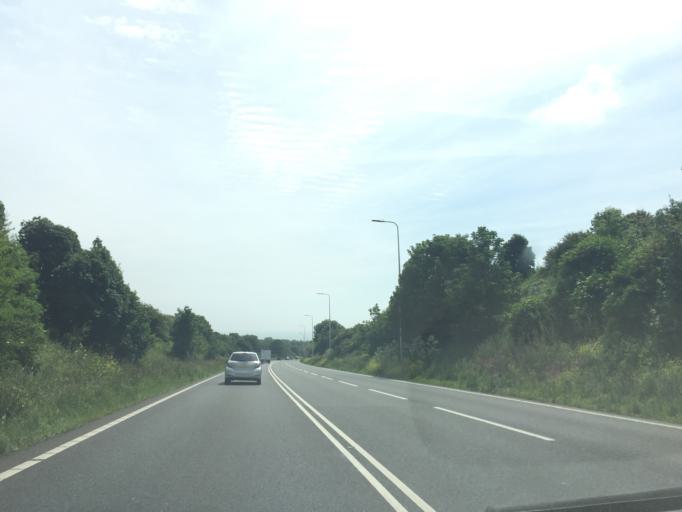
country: GB
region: England
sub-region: Kent
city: Dover
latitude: 51.1399
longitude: 1.3320
